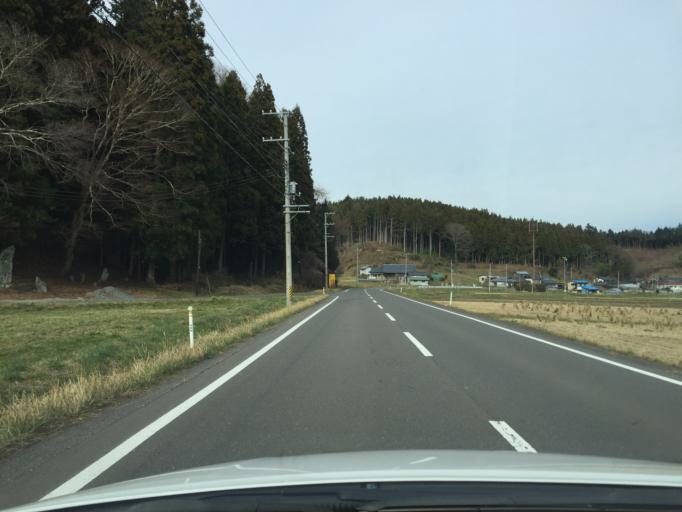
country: JP
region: Fukushima
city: Ishikawa
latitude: 37.2129
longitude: 140.6260
